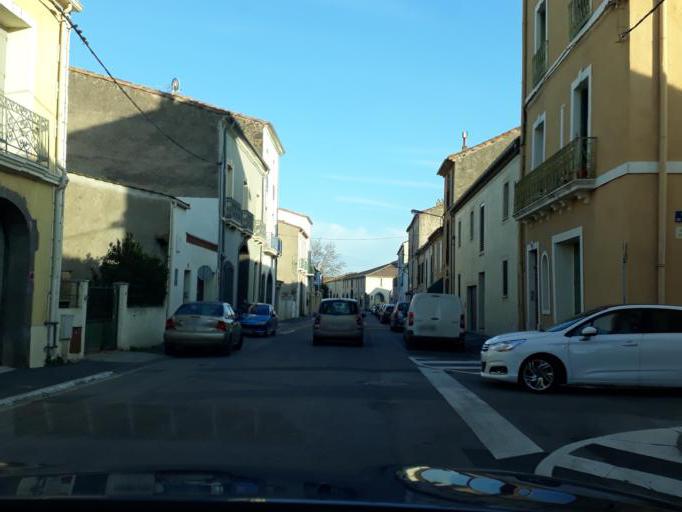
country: FR
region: Languedoc-Roussillon
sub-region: Departement de l'Herault
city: Marseillan
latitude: 43.3549
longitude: 3.5313
